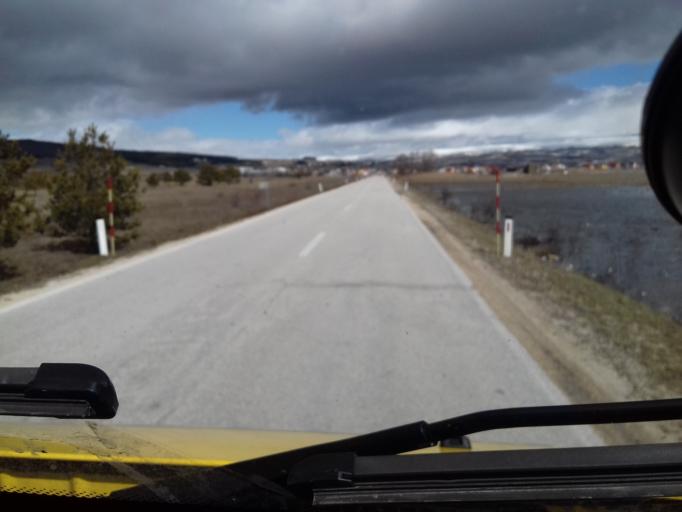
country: BA
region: Federation of Bosnia and Herzegovina
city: Tomislavgrad
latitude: 43.6842
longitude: 17.2049
